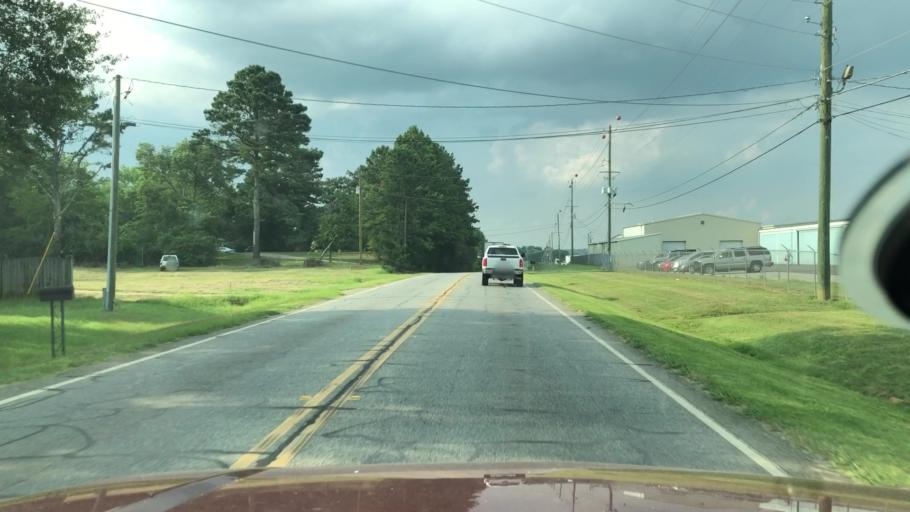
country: US
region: Georgia
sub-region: Bartow County
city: Cartersville
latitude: 34.1228
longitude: -84.8508
